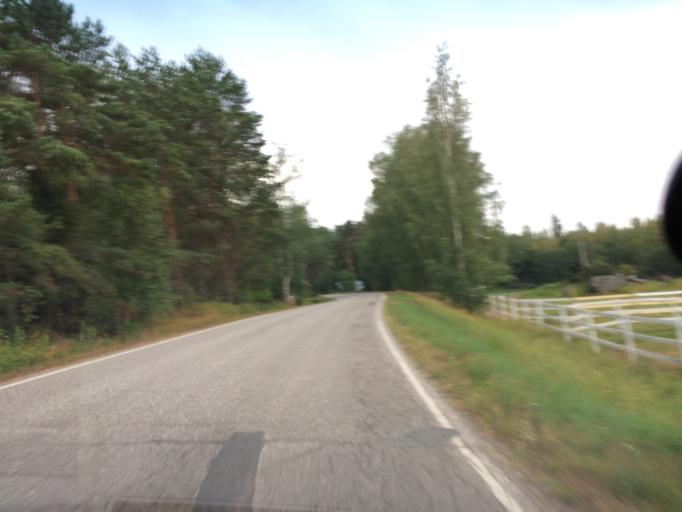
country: FI
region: Pirkanmaa
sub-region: Tampere
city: Luopioinen
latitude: 61.2546
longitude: 24.7071
